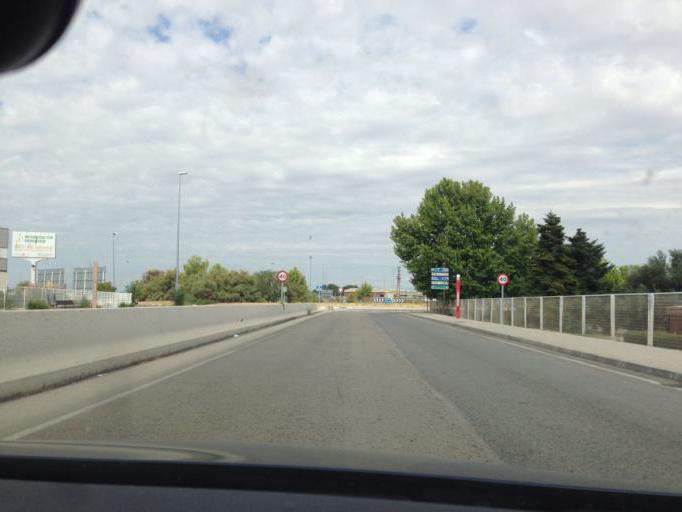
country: ES
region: Madrid
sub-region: Provincia de Madrid
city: Alcala de Henares
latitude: 40.4997
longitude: -3.3944
